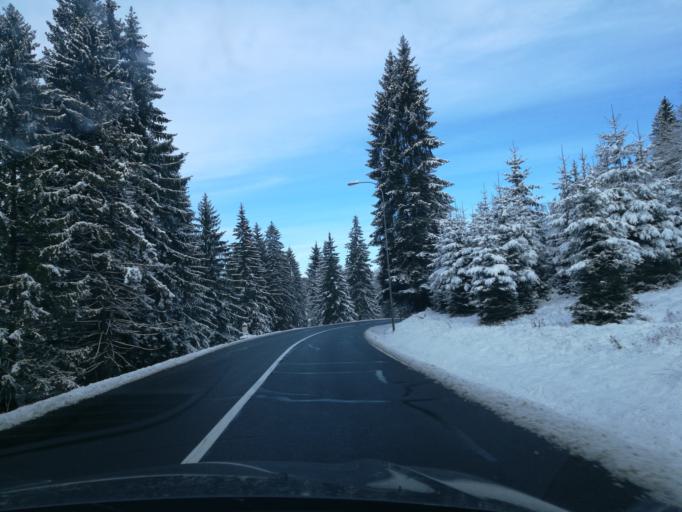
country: RO
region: Brasov
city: Brasov
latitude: 45.6052
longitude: 25.5544
